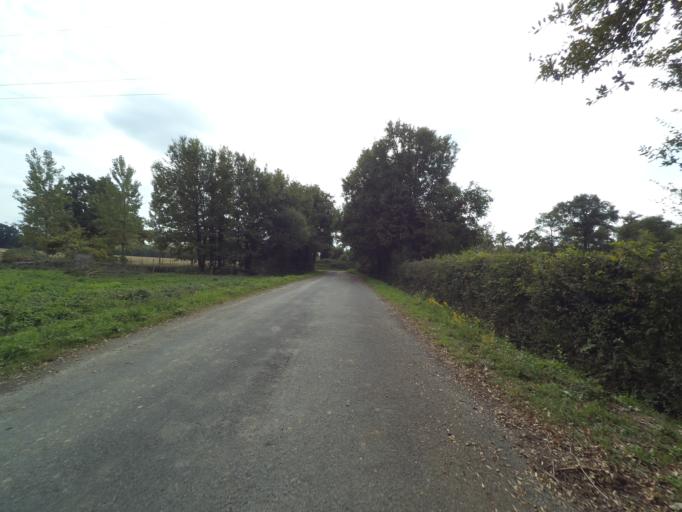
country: FR
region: Pays de la Loire
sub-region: Departement de la Vendee
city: Bouffere
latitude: 46.9783
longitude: -1.3519
